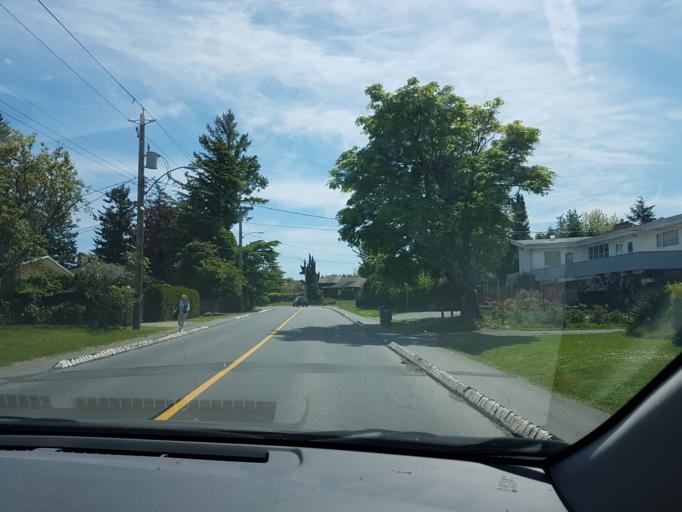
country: CA
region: British Columbia
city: Oak Bay
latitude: 48.4868
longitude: -123.3119
